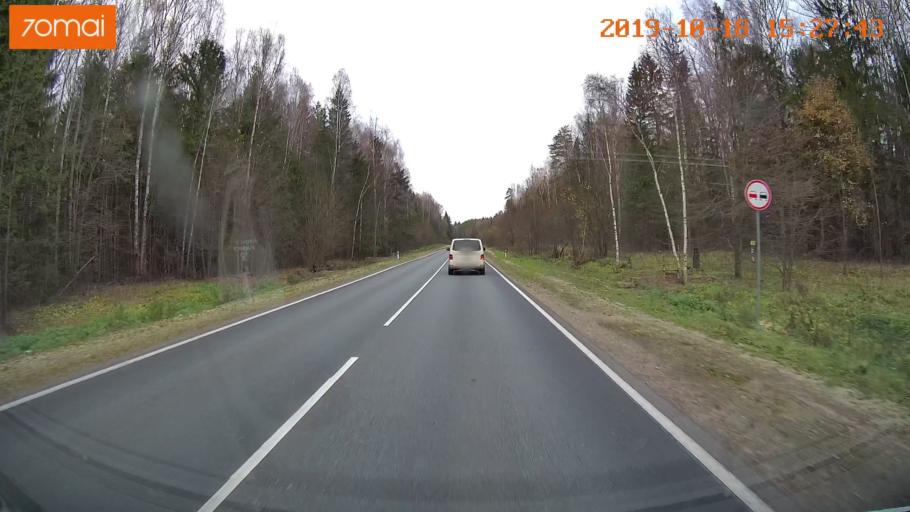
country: RU
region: Vladimir
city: Anopino
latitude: 55.7570
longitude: 40.6720
